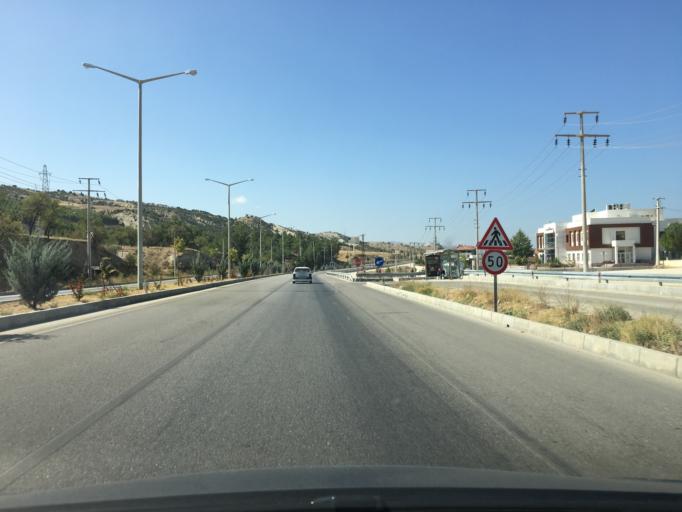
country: TR
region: Burdur
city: Burdur
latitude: 37.7535
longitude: 30.3341
